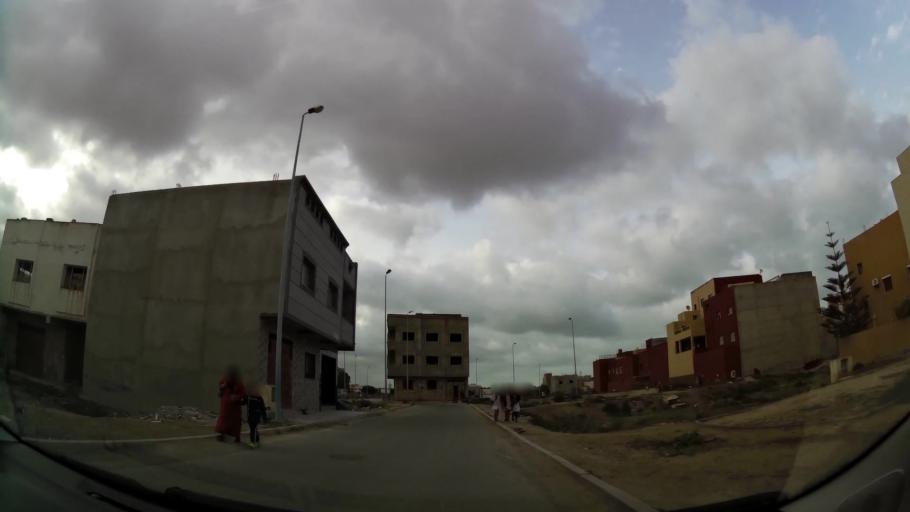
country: MA
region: Oriental
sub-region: Nador
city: Nador
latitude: 35.1588
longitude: -2.9143
